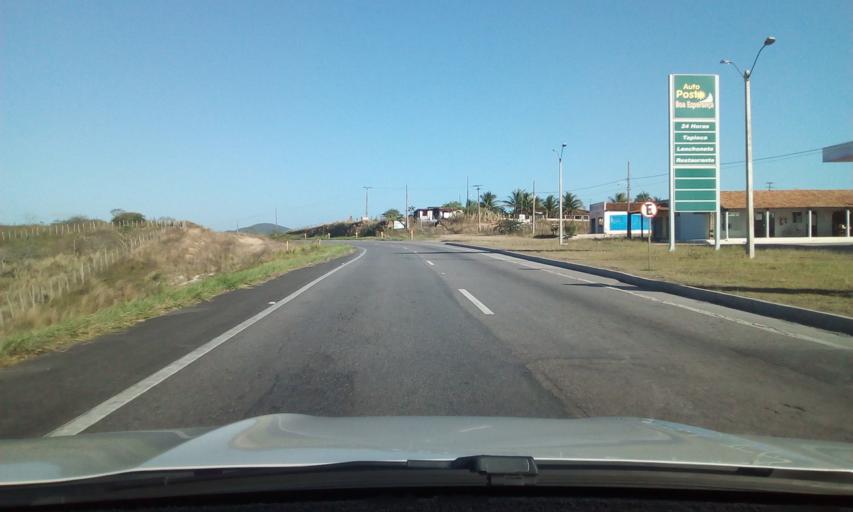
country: BR
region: Paraiba
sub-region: Gurinhem
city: Gurinhem
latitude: -7.1678
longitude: -35.3340
